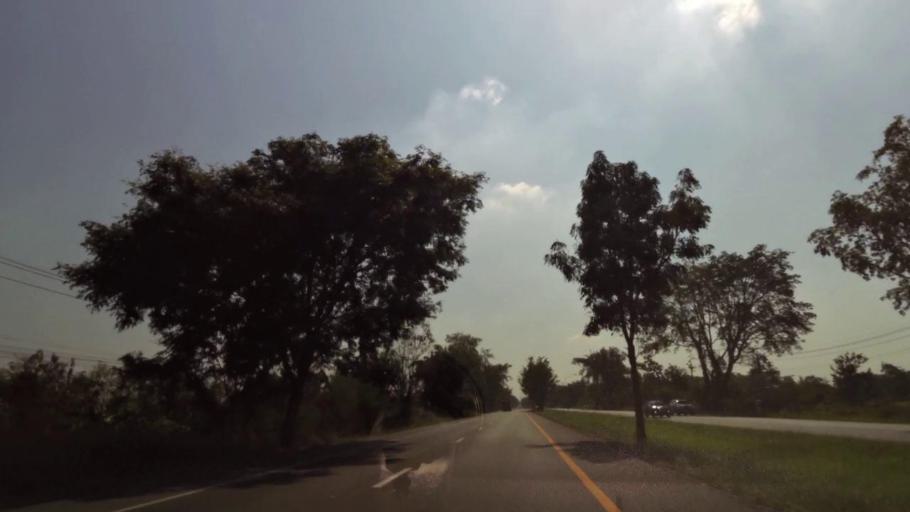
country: TH
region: Phichit
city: Bueng Na Rang
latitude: 16.2232
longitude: 100.1263
